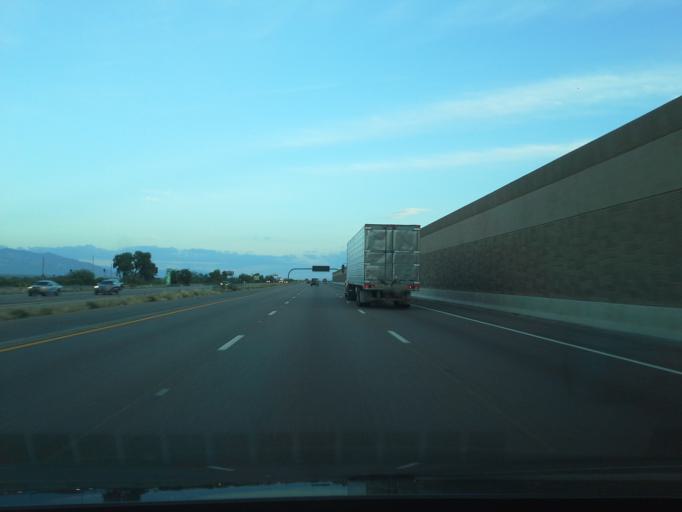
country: US
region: Arizona
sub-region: Pima County
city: Marana
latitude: 32.4562
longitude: -111.2082
